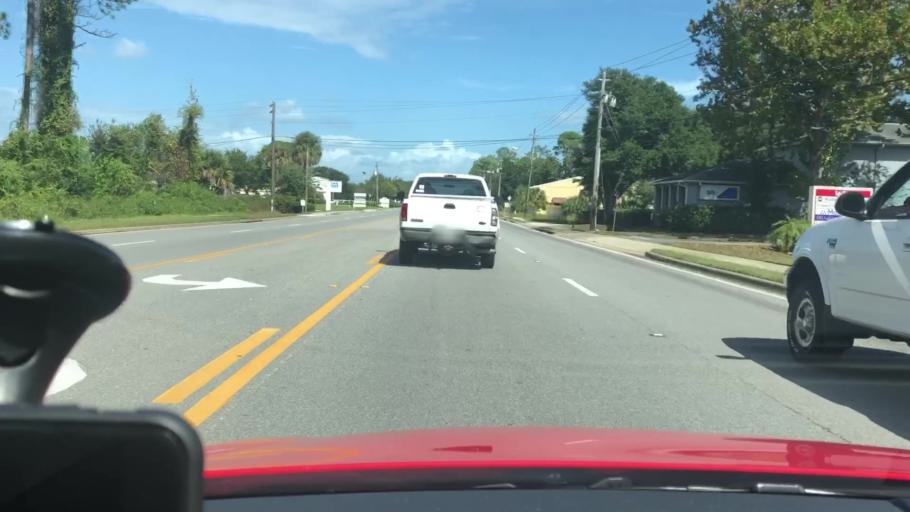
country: US
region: Florida
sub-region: Volusia County
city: Holly Hill
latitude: 29.2112
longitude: -81.0677
